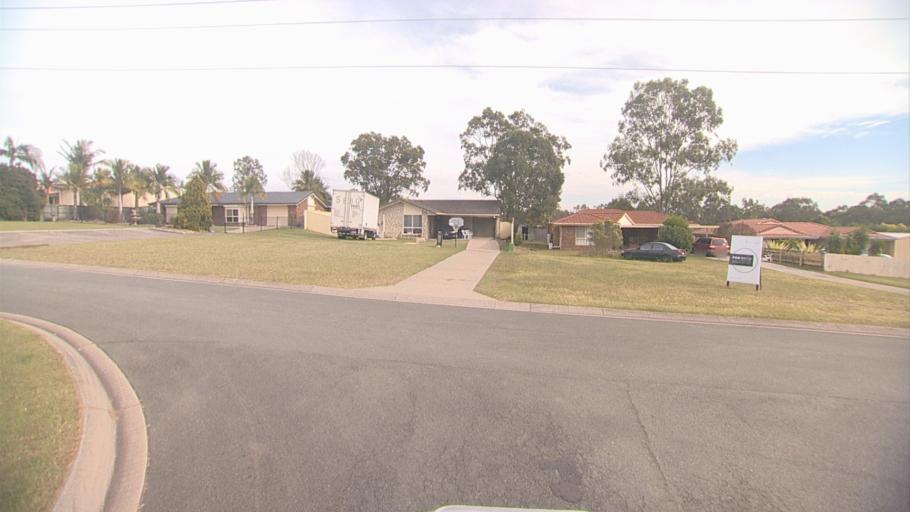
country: AU
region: Queensland
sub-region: Logan
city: Beenleigh
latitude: -27.7009
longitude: 153.1776
